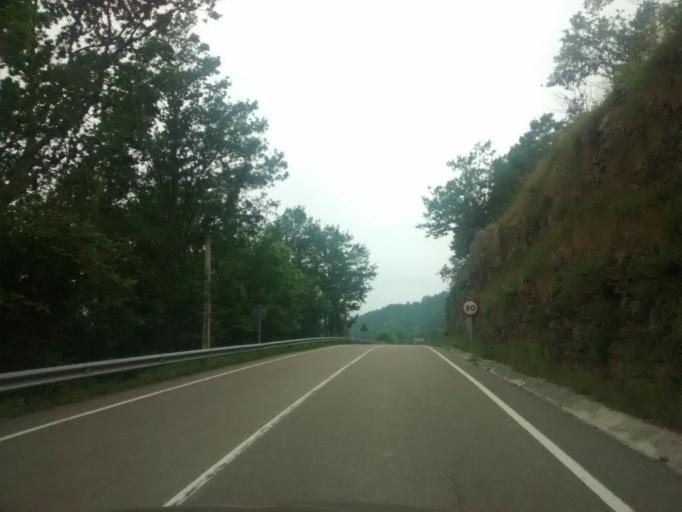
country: ES
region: Cantabria
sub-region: Provincia de Cantabria
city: Ruente
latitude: 43.1660
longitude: -4.2689
